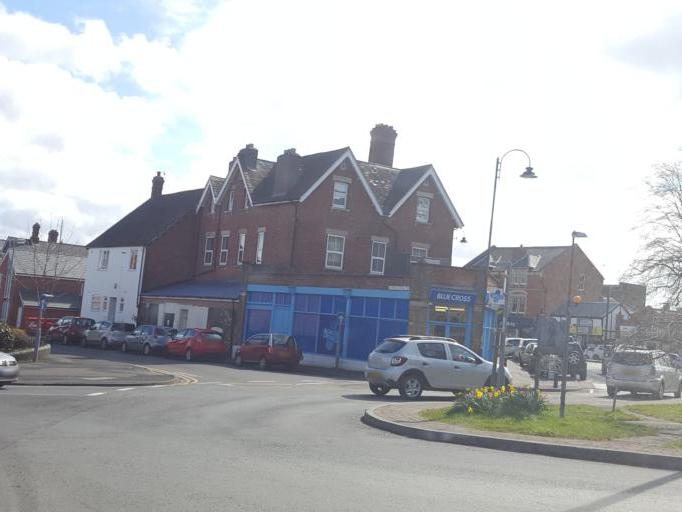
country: GB
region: England
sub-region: Worcestershire
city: Great Malvern
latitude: 52.1091
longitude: -2.3122
